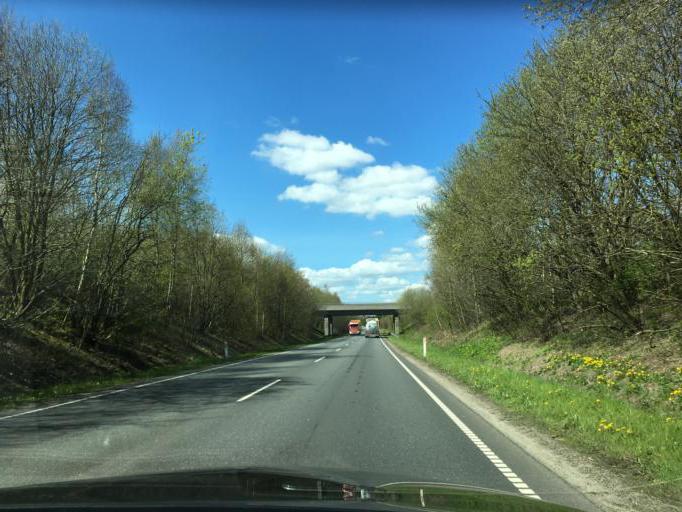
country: DK
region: Central Jutland
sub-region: Hedensted Kommune
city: Hedensted
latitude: 55.8402
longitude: 9.7560
